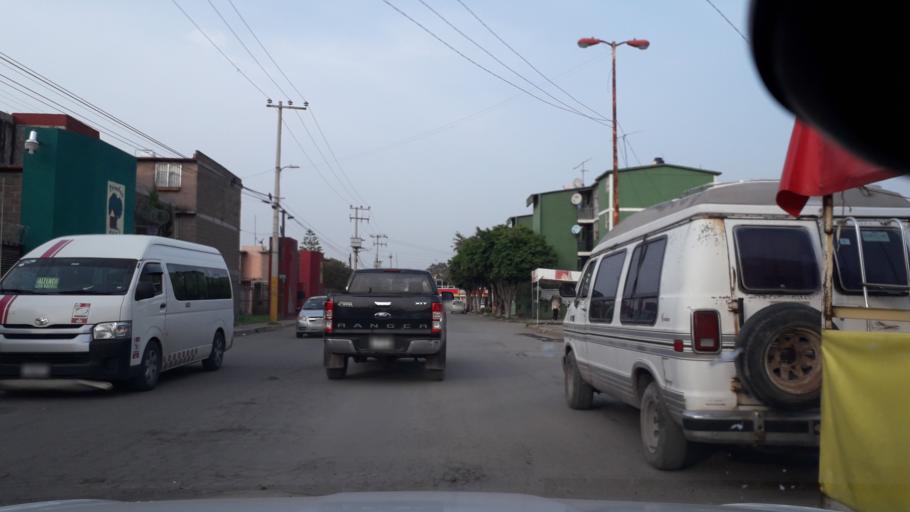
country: MX
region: Mexico
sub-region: Jaltenco
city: Alborada Jaltenco
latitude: 19.6587
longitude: -99.0707
